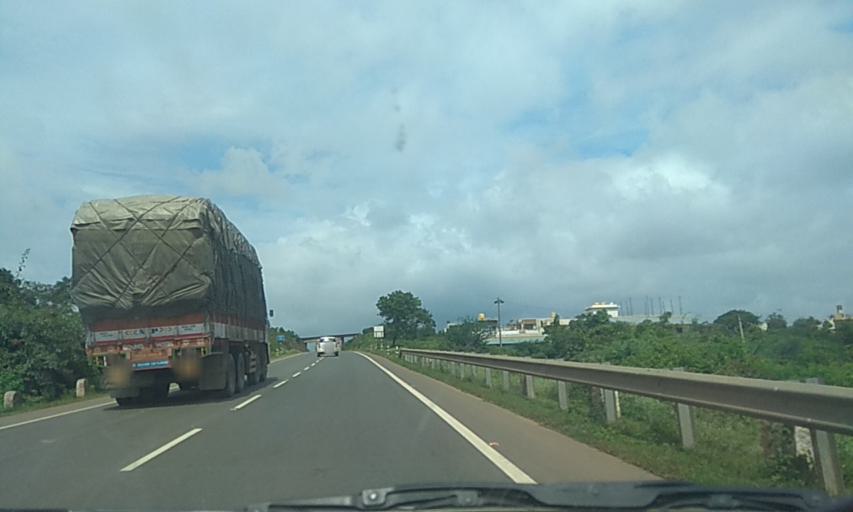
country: IN
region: Karnataka
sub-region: Dharwad
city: Hubli
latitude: 15.3297
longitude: 75.1170
